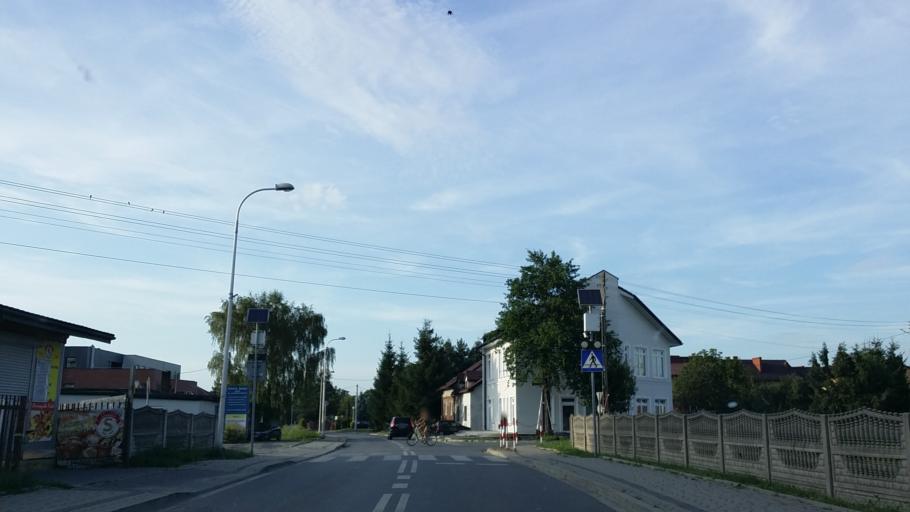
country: PL
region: Lesser Poland Voivodeship
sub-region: Powiat oswiecimski
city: Zator
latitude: 49.9930
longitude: 19.4327
